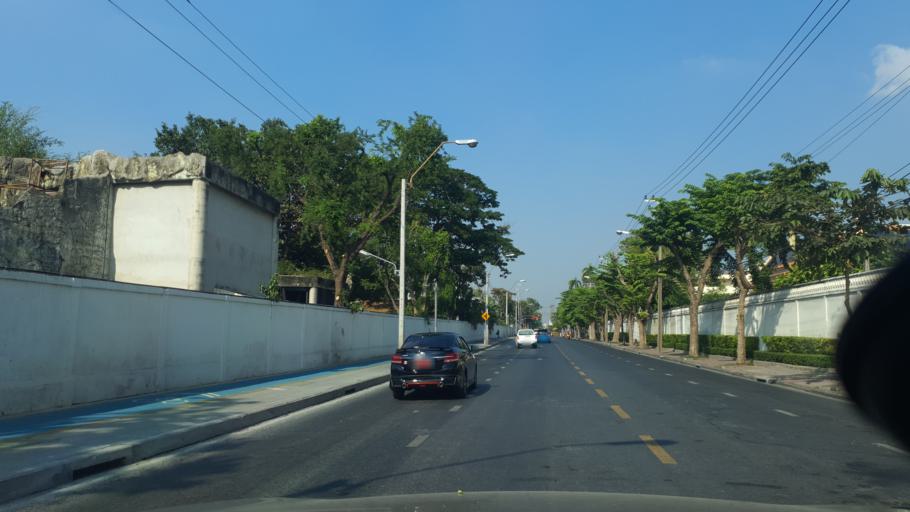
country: TH
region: Bangkok
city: Dusit
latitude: 13.7744
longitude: 100.5173
